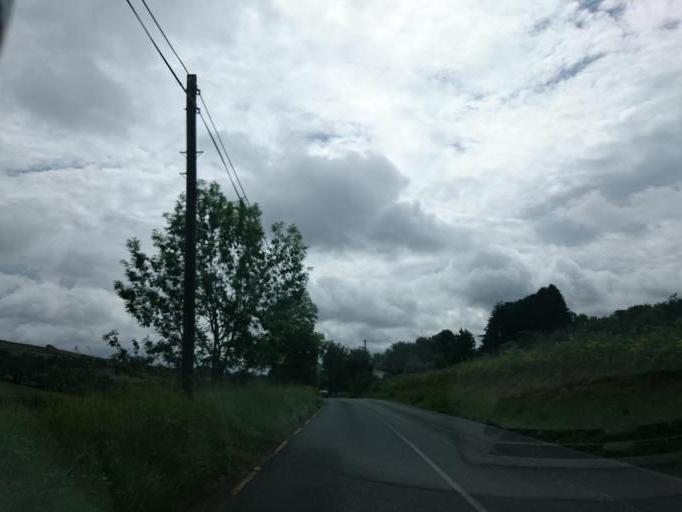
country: IE
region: Leinster
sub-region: Wicklow
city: Carnew
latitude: 52.8050
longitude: -6.4778
